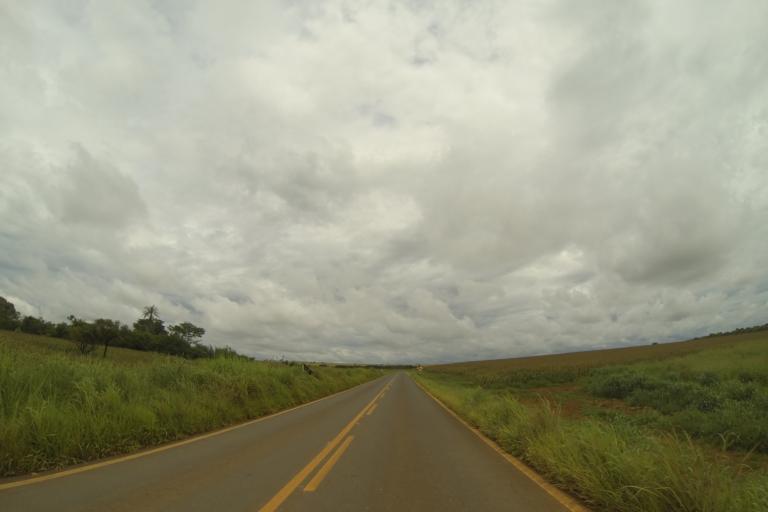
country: BR
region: Minas Gerais
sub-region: Bambui
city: Bambui
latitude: -20.0981
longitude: -46.0926
